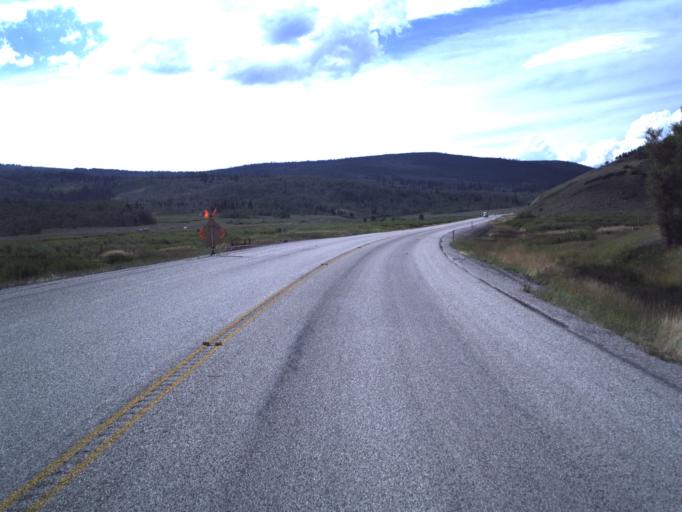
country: US
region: Utah
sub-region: Wasatch County
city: Heber
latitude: 40.2832
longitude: -111.2368
